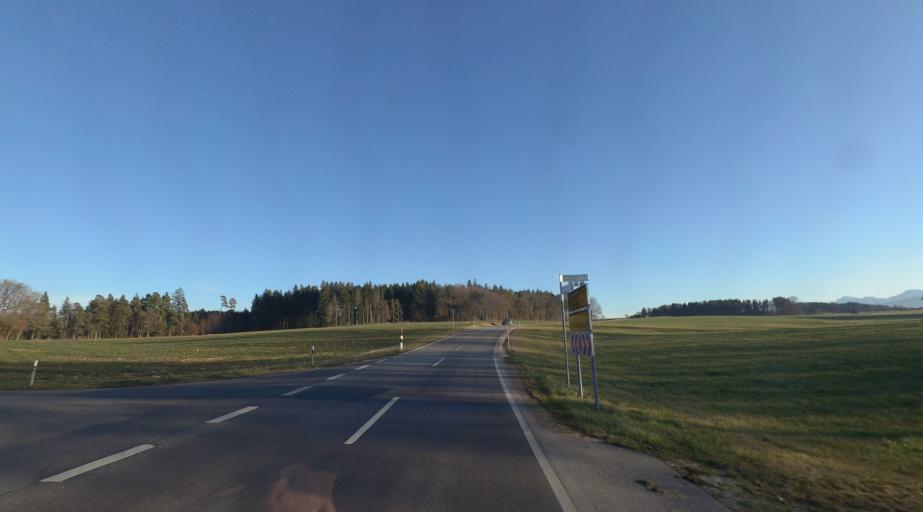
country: DE
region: Bavaria
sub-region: Upper Bavaria
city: Taching am See
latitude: 47.9913
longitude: 12.7651
